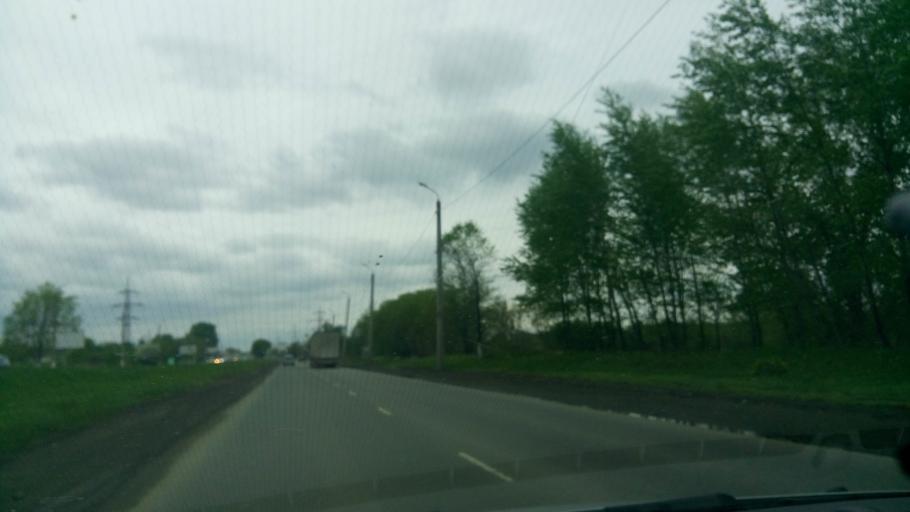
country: RU
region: Chelyabinsk
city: Dolgoderevenskoye
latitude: 55.2447
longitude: 61.3596
